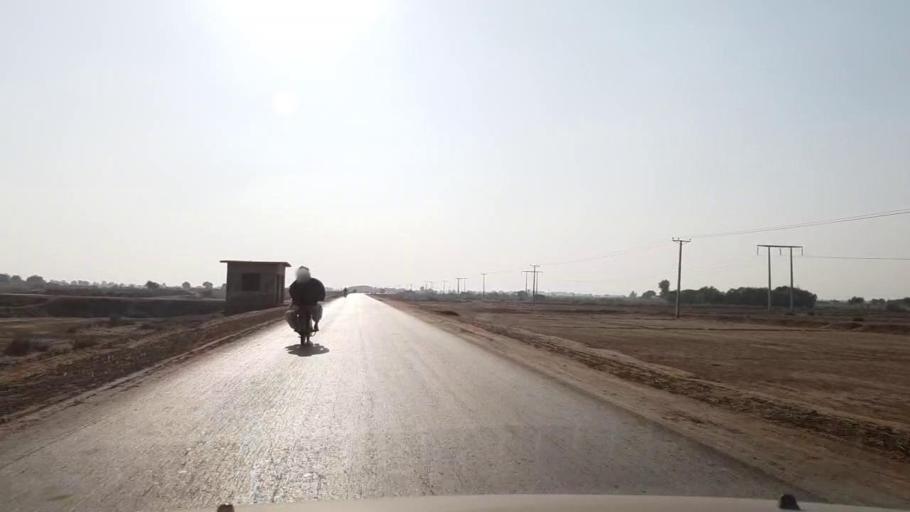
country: PK
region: Sindh
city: Tando Muhammad Khan
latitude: 25.0240
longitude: 68.4173
